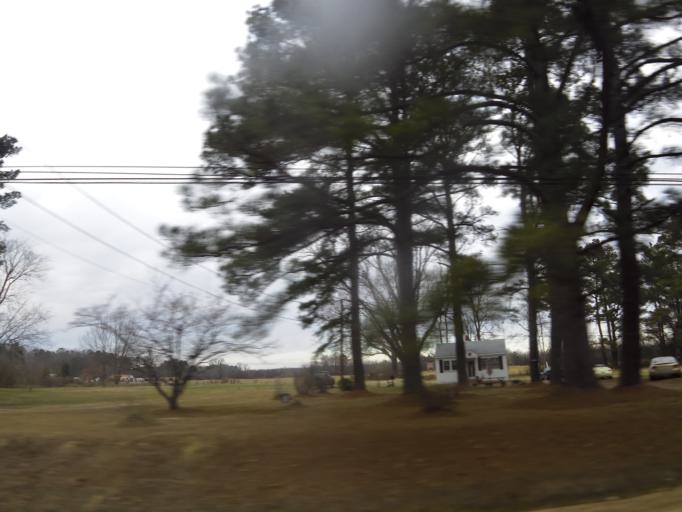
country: US
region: North Carolina
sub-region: Hertford County
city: Murfreesboro
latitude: 36.3234
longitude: -77.2277
